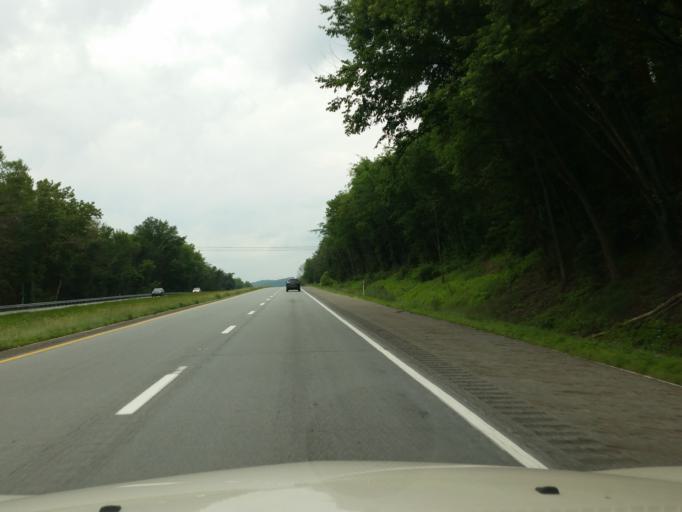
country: US
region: Pennsylvania
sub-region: Perry County
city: Newport
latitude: 40.5197
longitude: -77.1298
